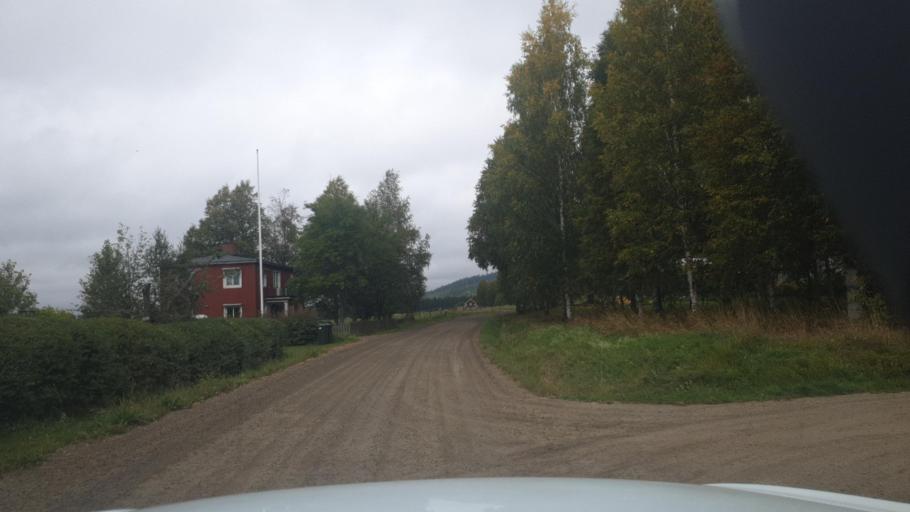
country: SE
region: Vaermland
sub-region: Sunne Kommun
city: Sunne
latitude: 59.7992
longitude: 13.1045
